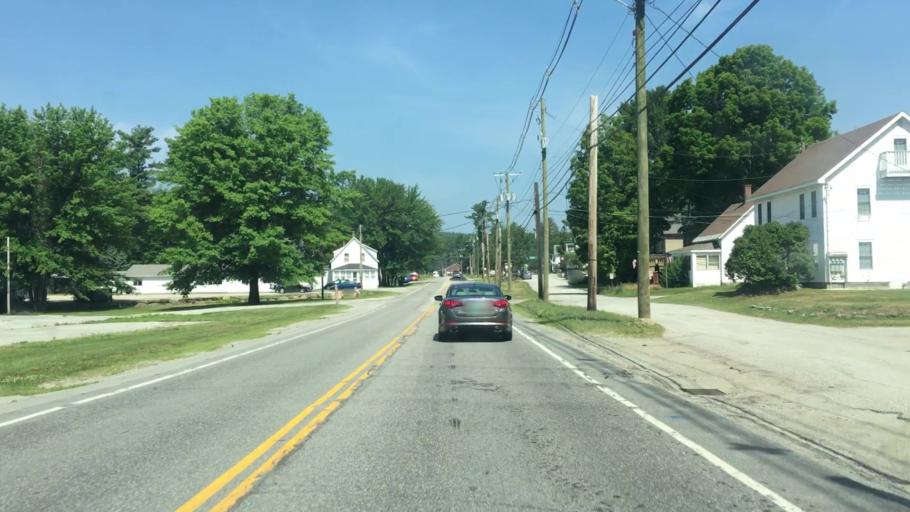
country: US
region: New Hampshire
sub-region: Sullivan County
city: Newport
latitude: 43.3761
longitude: -72.1380
